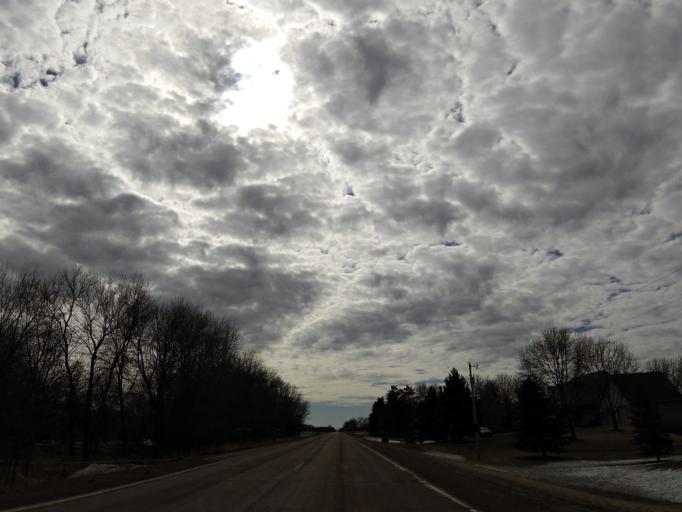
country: US
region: Minnesota
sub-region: Scott County
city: Prior Lake
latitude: 44.6579
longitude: -93.5165
